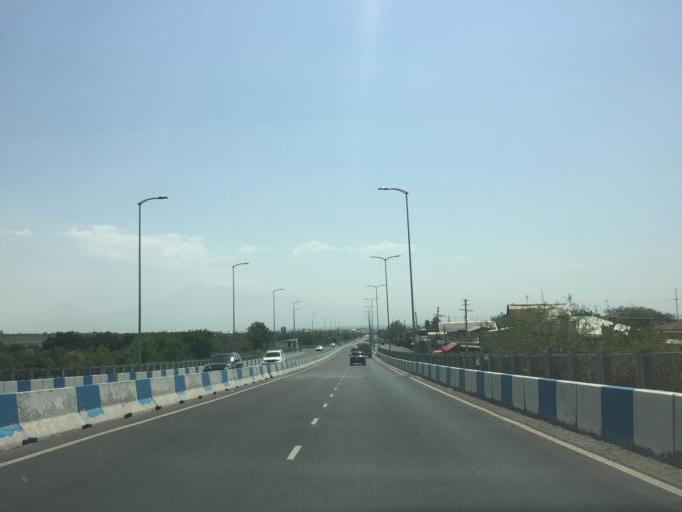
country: AM
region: Ararat
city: Norabats'
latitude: 40.1222
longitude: 44.4840
